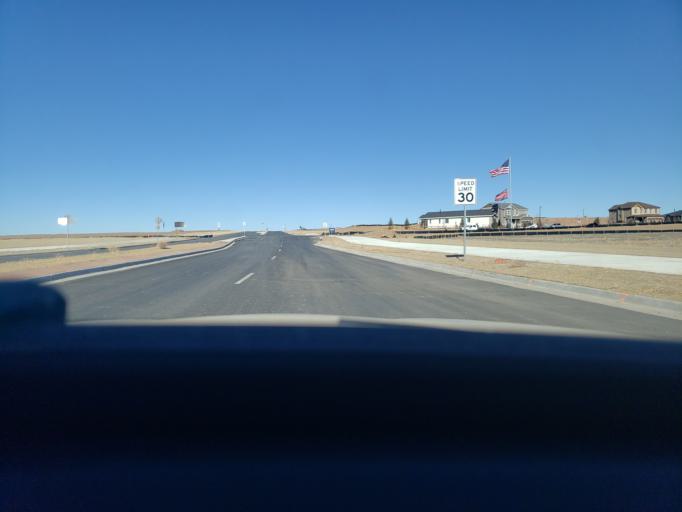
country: US
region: Colorado
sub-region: Adams County
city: Aurora
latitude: 39.7717
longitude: -104.7065
